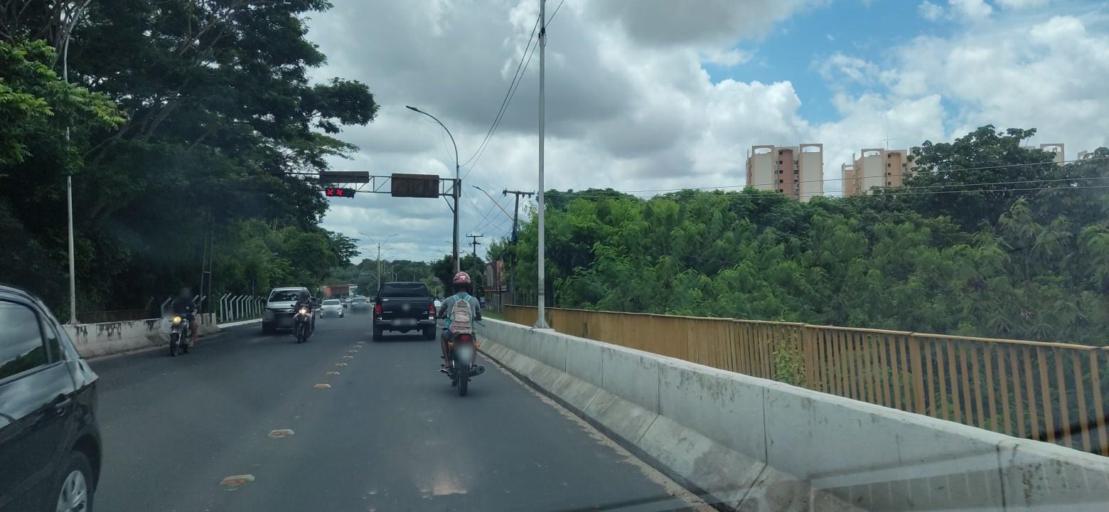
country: BR
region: Piaui
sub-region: Teresina
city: Teresina
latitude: -5.0634
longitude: -42.8064
